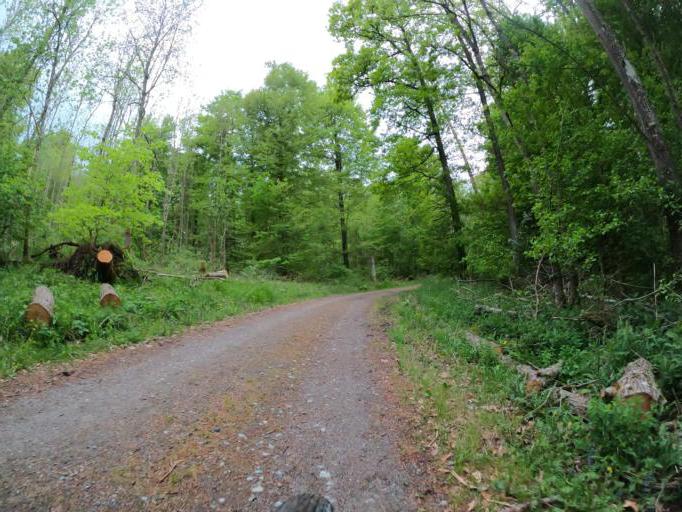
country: DE
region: Baden-Wuerttemberg
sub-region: Regierungsbezirk Stuttgart
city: Aidlingen
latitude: 48.6974
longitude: 8.9159
